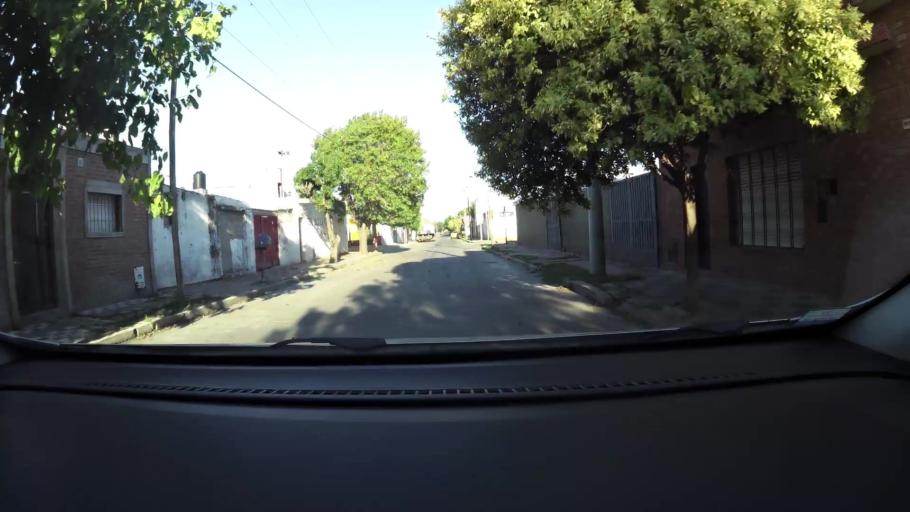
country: AR
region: Cordoba
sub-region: Departamento de Capital
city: Cordoba
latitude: -31.3771
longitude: -64.1979
